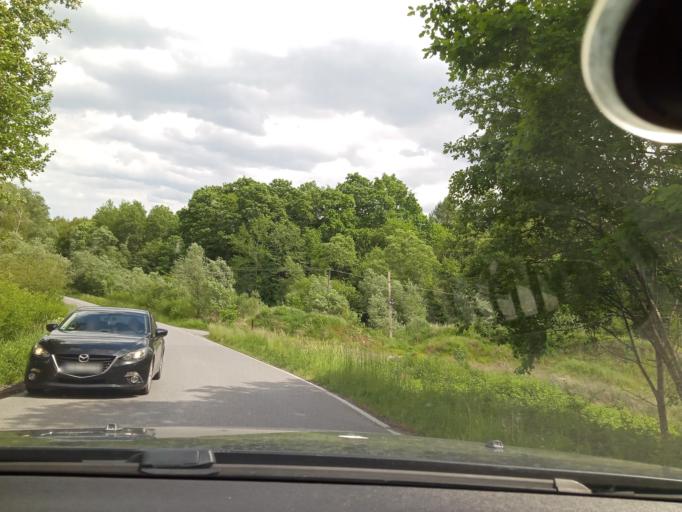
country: PL
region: Lesser Poland Voivodeship
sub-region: Powiat bochenski
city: Lapanow
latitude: 49.8526
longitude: 20.2568
